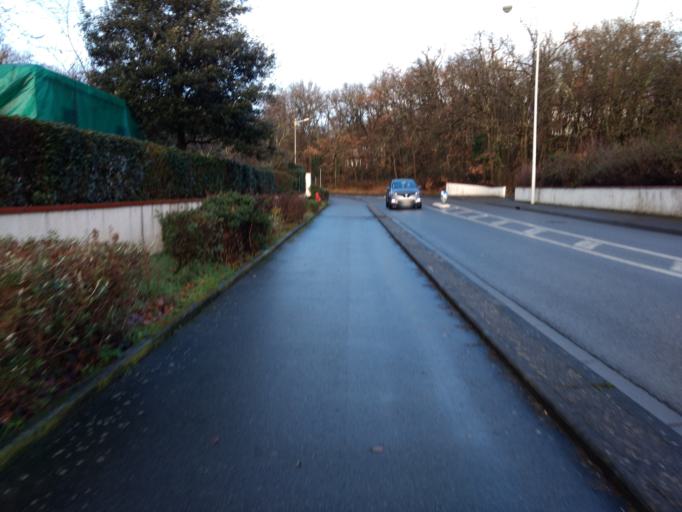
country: FR
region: Midi-Pyrenees
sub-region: Departement de la Haute-Garonne
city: Tournefeuille
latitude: 43.5922
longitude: 1.3383
